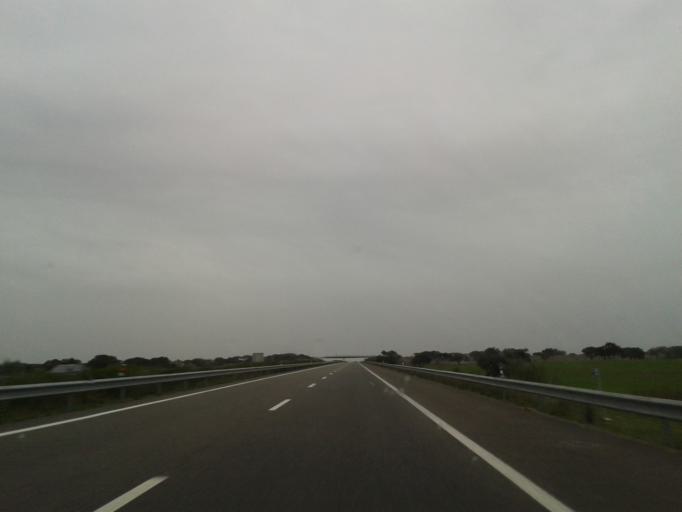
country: PT
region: Beja
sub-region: Ourique
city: Ourique
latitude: 37.5994
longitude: -8.1729
